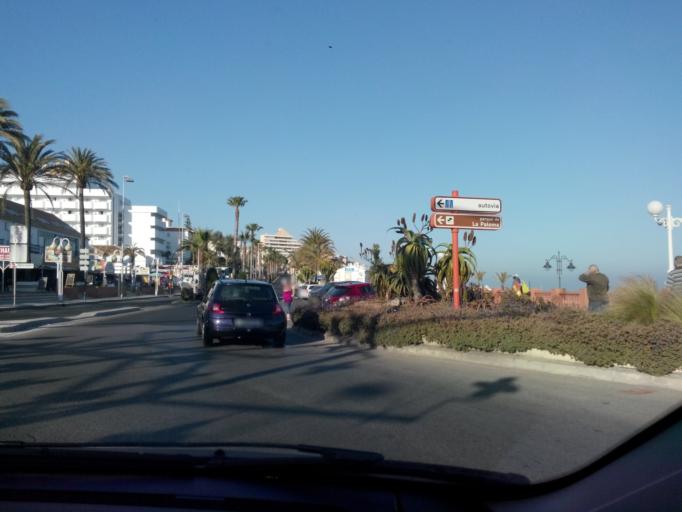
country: ES
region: Andalusia
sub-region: Provincia de Malaga
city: Torremolinos
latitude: 36.5913
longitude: -4.5261
